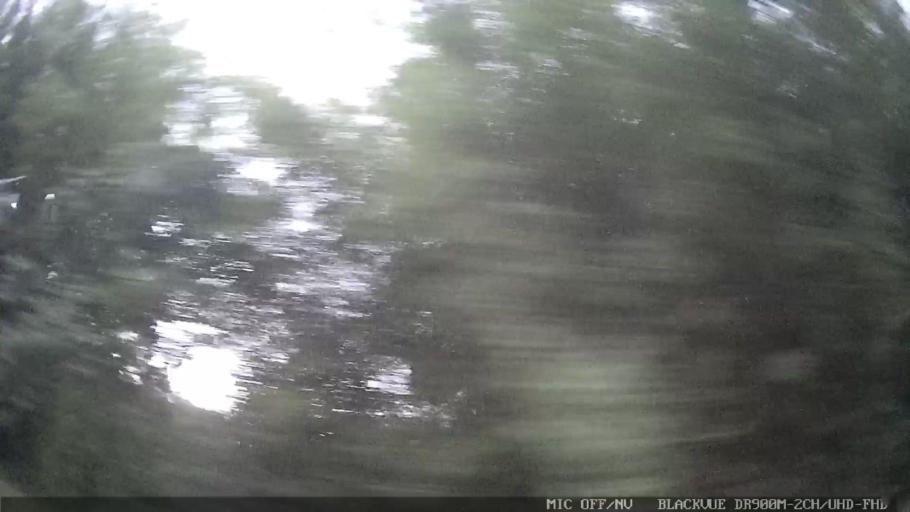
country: BR
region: Sao Paulo
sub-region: Itatiba
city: Itatiba
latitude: -22.8981
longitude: -46.7858
